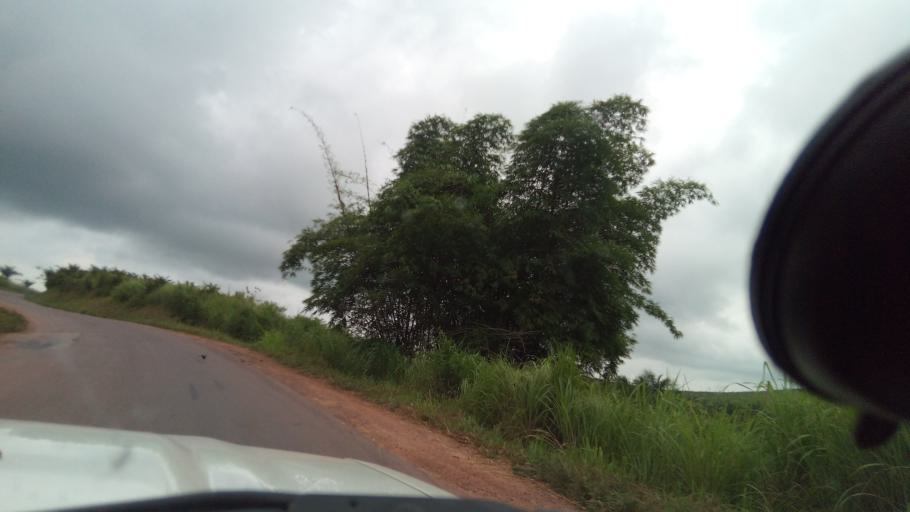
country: CD
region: Bas-Congo
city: Kasangulu
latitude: -4.9398
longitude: 15.1485
